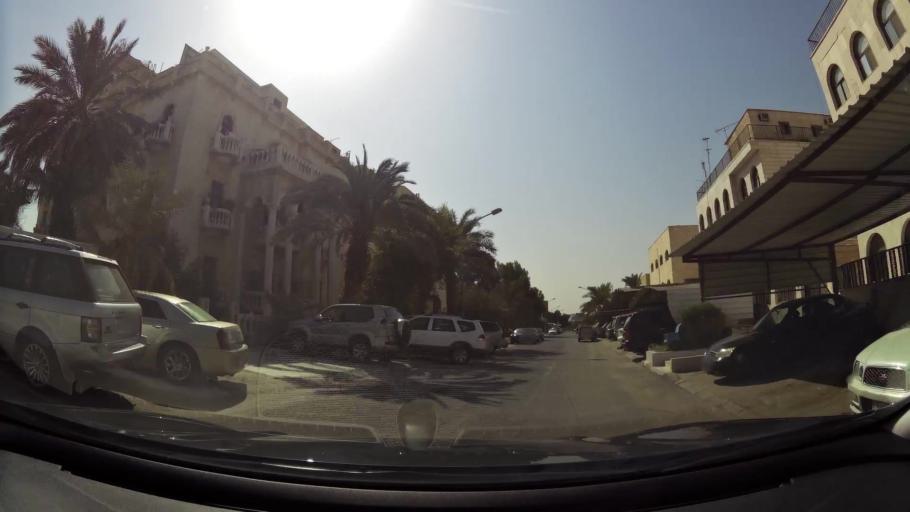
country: KW
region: Muhafazat Hawalli
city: Salwa
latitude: 29.2806
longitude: 48.0824
